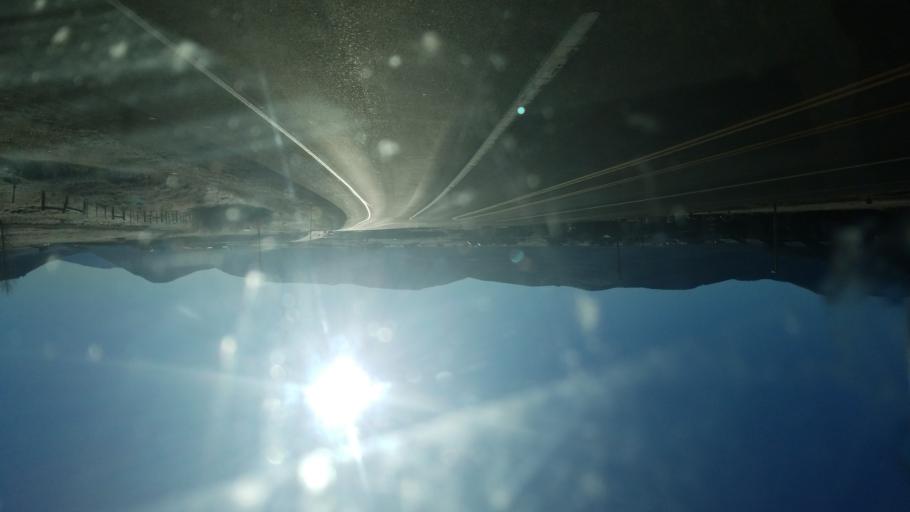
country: US
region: Colorado
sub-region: Gunnison County
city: Crested Butte
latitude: 38.8555
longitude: -106.9610
